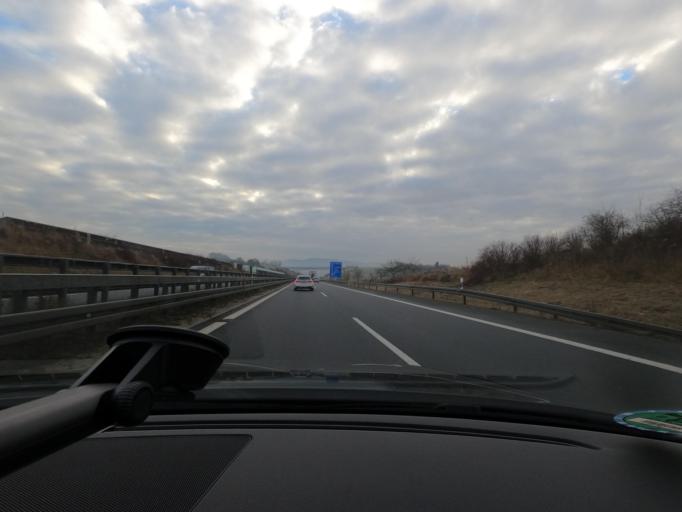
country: DE
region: Bavaria
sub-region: Upper Franconia
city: Lichtenfels
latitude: 50.1542
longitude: 11.0229
